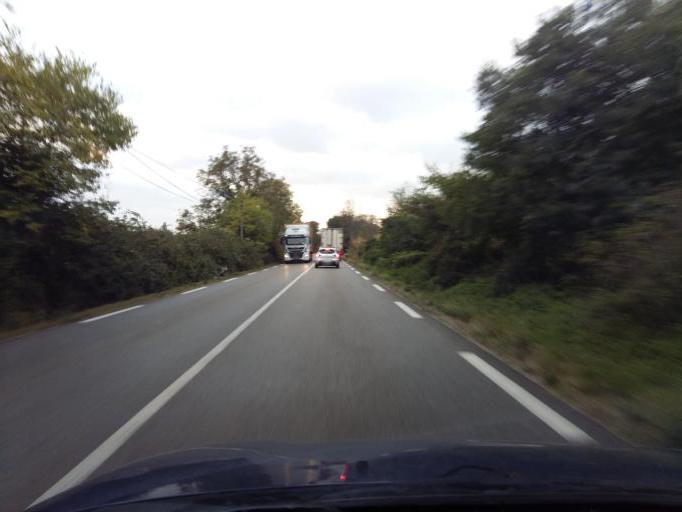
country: FR
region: Provence-Alpes-Cote d'Azur
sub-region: Departement des Bouches-du-Rhone
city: Miramas
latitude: 43.6192
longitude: 5.0147
